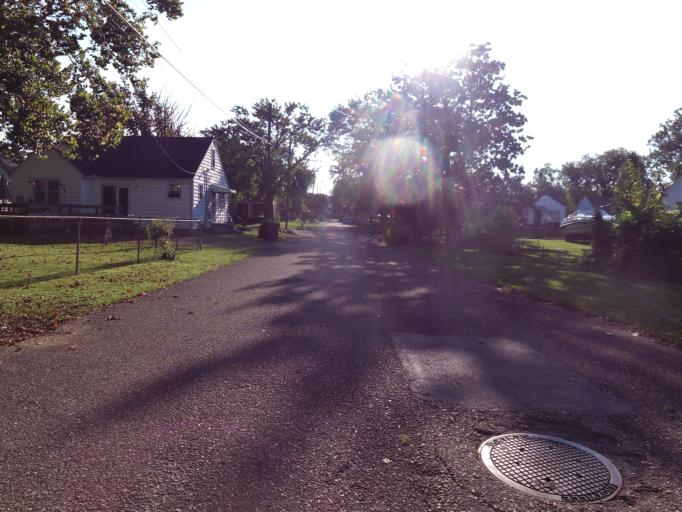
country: US
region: Tennessee
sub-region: Knox County
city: Knoxville
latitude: 36.0060
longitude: -83.9167
